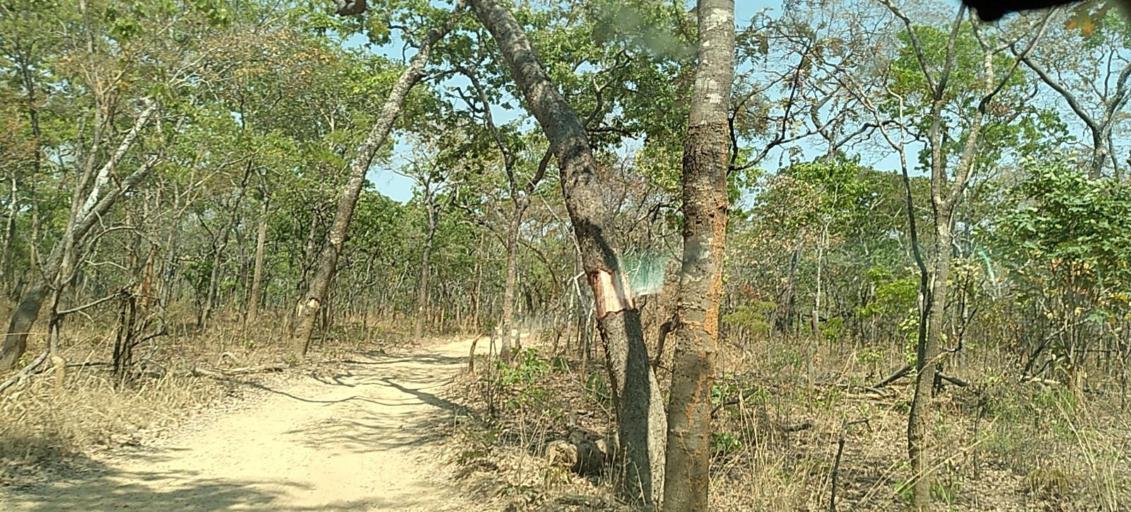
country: ZM
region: North-Western
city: Kasempa
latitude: -13.3921
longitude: 25.6255
